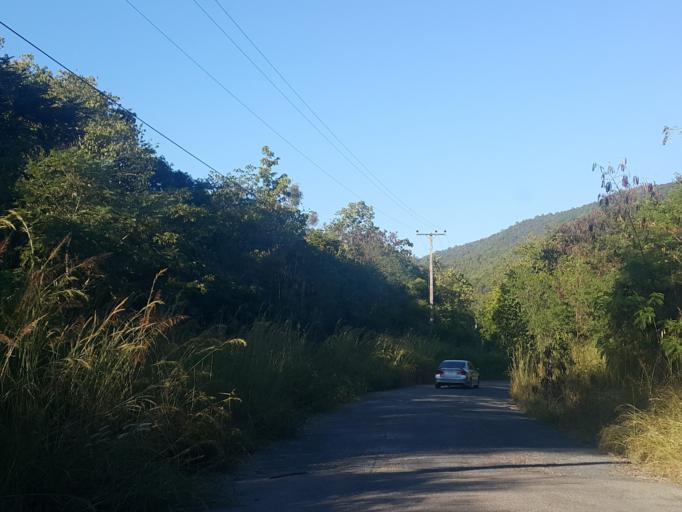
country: TH
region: Chiang Mai
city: San Sai
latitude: 18.9315
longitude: 99.1373
